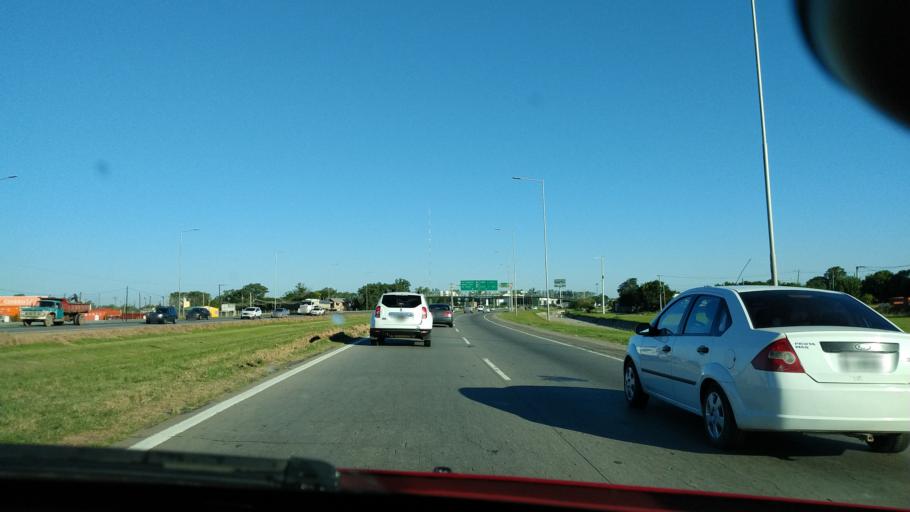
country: AR
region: Cordoba
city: Malvinas Argentinas
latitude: -31.3661
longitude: -64.1320
